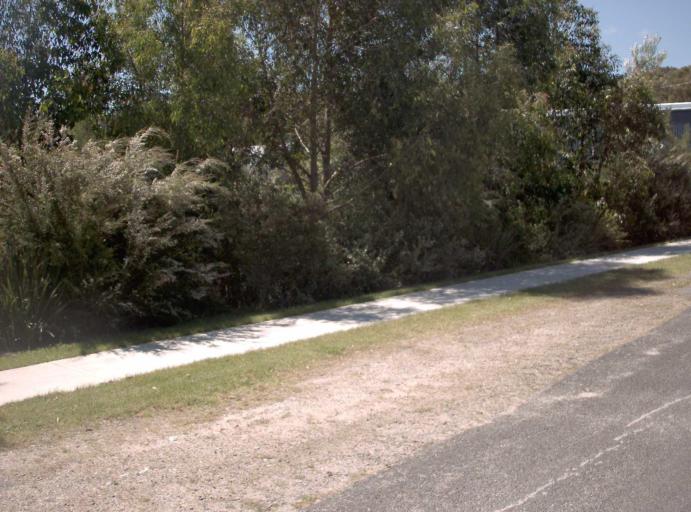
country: AU
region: Victoria
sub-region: Latrobe
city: Morwell
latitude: -38.6504
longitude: 146.2043
